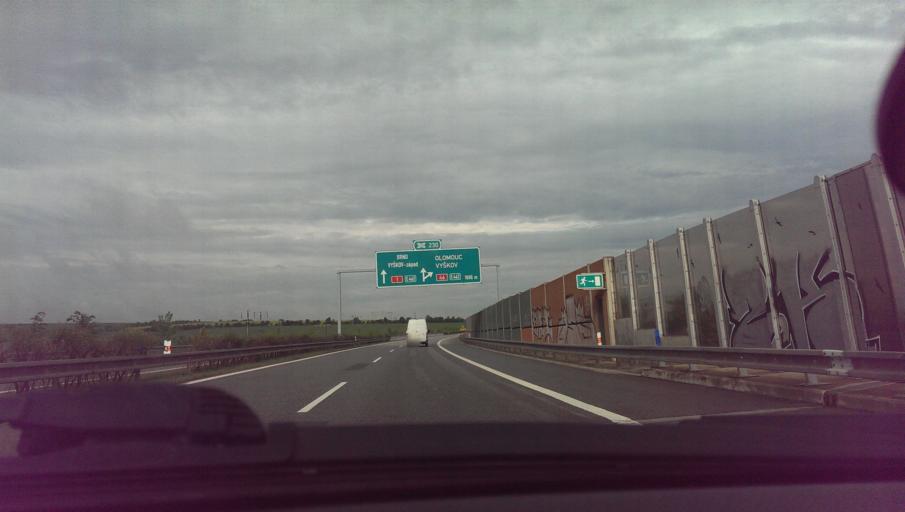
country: CZ
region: South Moravian
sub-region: Okres Vyskov
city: Vyskov
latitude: 49.2733
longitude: 17.0426
